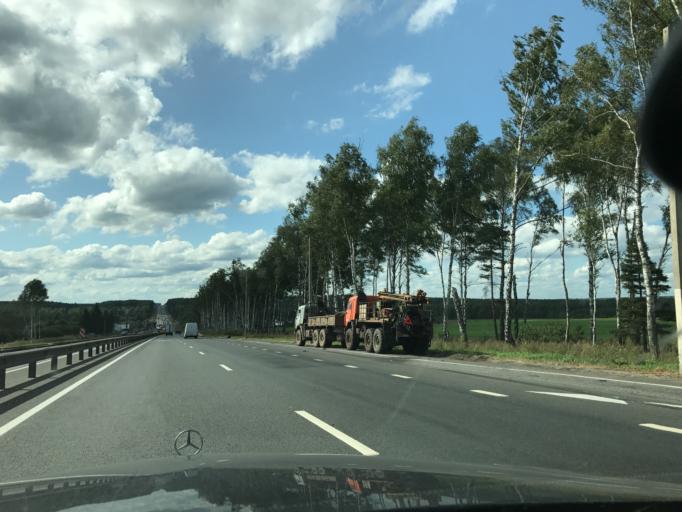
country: RU
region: Vladimir
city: Melekhovo
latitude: 56.2129
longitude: 41.3389
